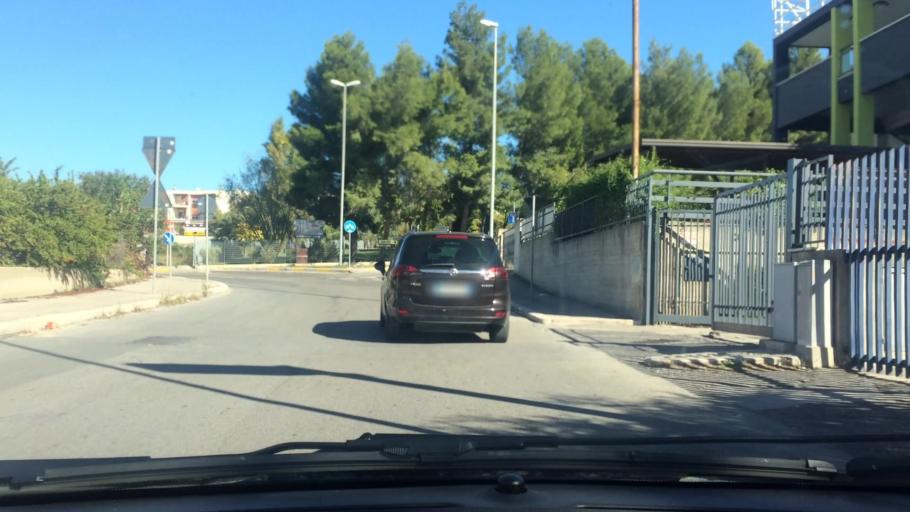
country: IT
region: Basilicate
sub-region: Provincia di Matera
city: Matera
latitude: 40.6746
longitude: 16.5765
